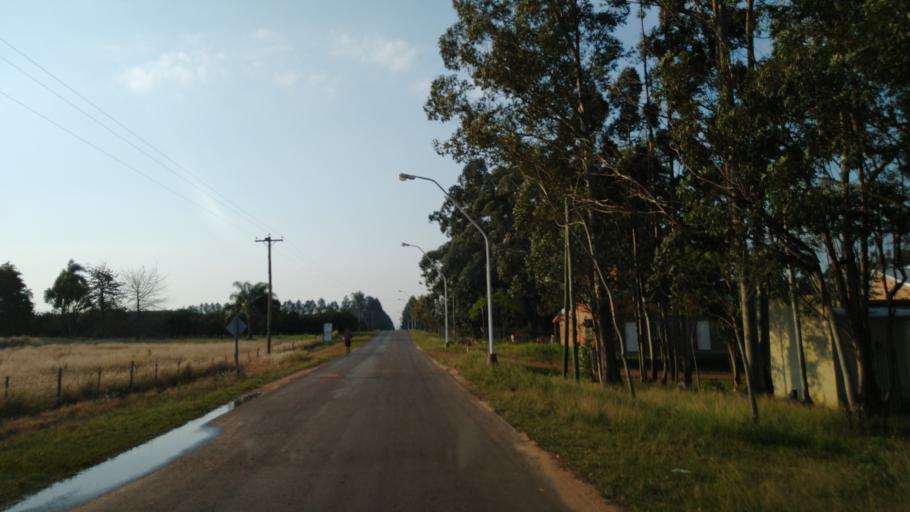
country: AR
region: Entre Rios
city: Santa Ana
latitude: -30.9119
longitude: -57.9266
